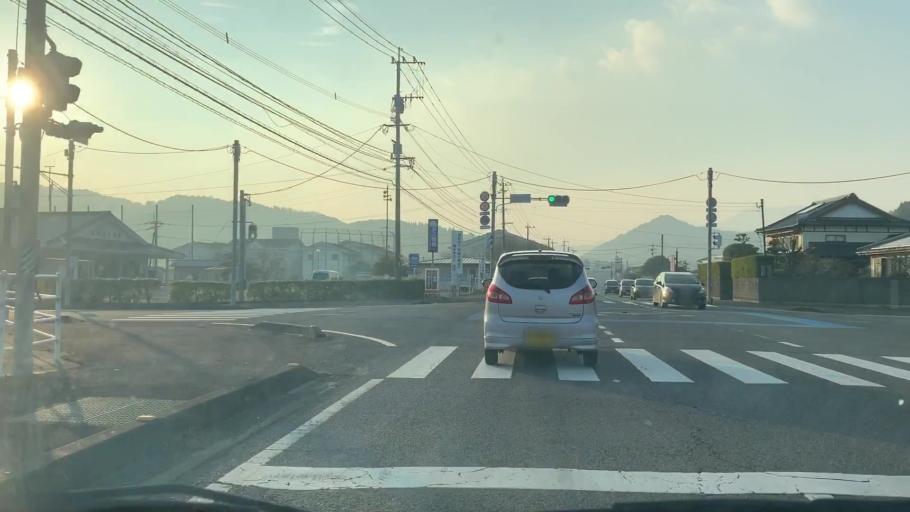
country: JP
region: Saga Prefecture
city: Takeocho-takeo
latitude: 33.2721
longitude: 130.1278
